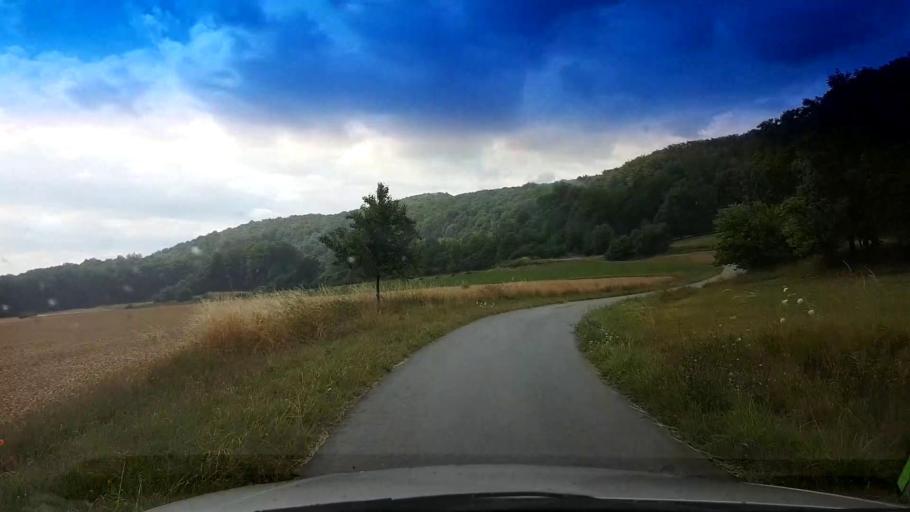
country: DE
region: Bavaria
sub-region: Upper Franconia
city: Schesslitz
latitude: 49.9817
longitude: 11.0812
